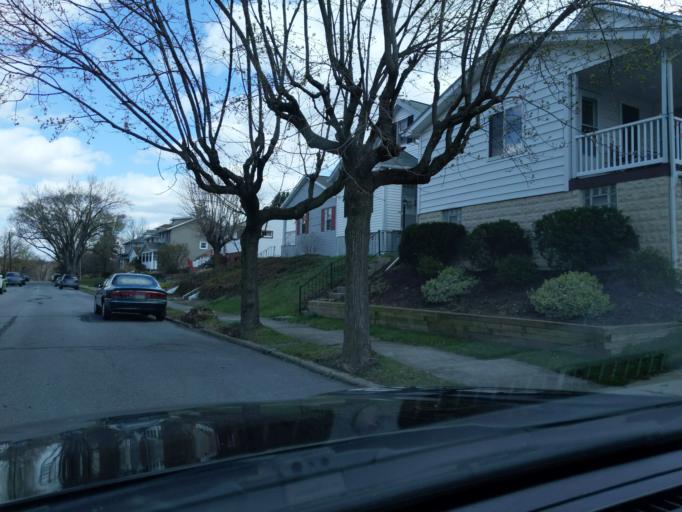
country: US
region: Pennsylvania
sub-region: Blair County
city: Altoona
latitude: 40.5320
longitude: -78.4017
